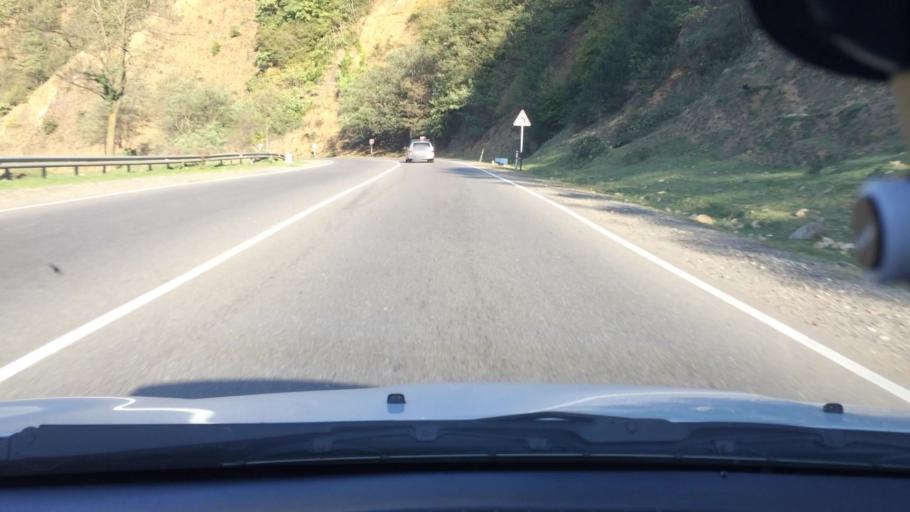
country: GE
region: Imereti
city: Kharagauli
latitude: 42.1142
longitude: 43.2868
